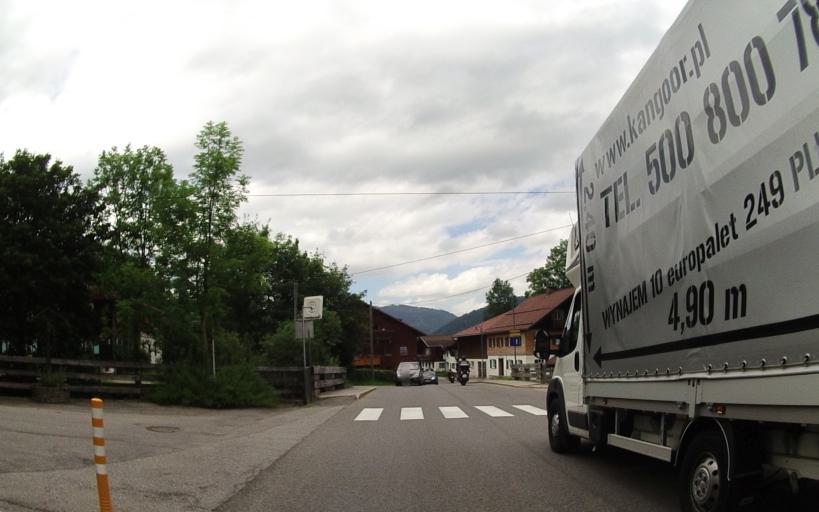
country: AT
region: Tyrol
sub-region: Politischer Bezirk Reutte
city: Schattwald
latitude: 47.5139
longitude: 10.4608
